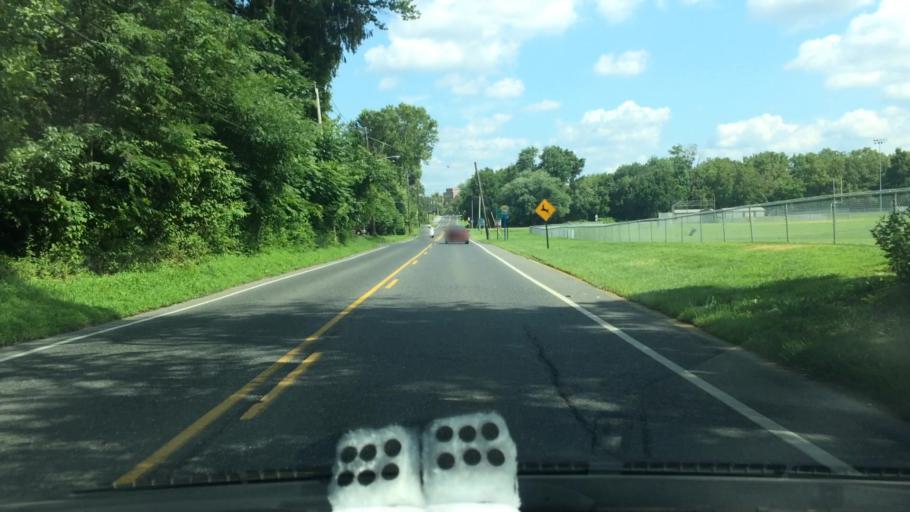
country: US
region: New Jersey
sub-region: Camden County
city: Blackwood
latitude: 39.7911
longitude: -75.0783
